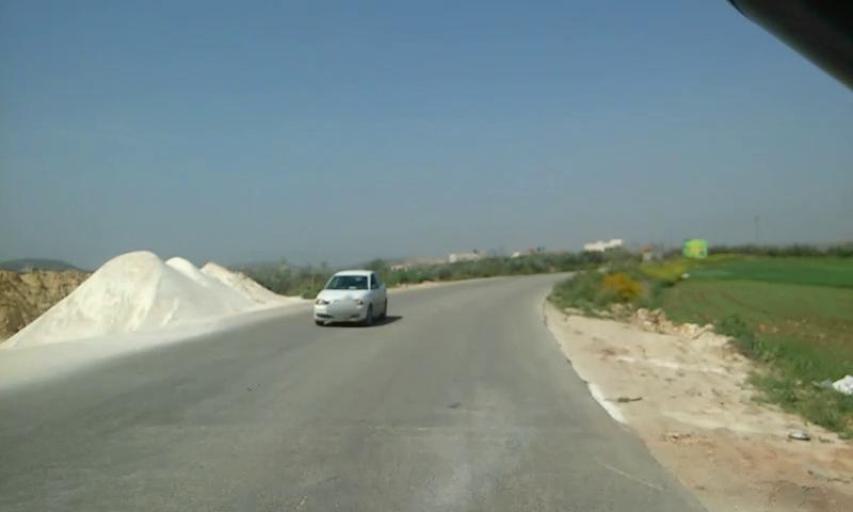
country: PS
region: West Bank
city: Az Zababidah
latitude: 32.3786
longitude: 35.3319
